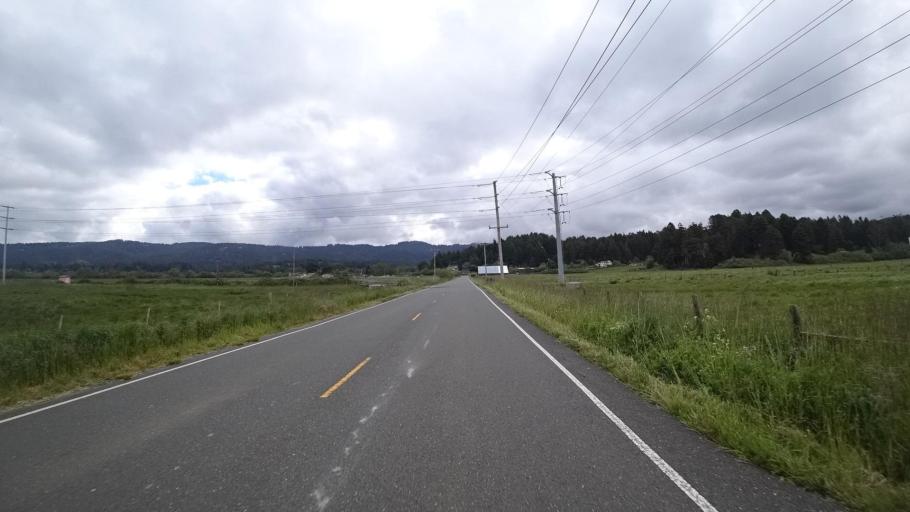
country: US
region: California
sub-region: Humboldt County
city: Bayside
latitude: 40.8350
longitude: -124.0787
